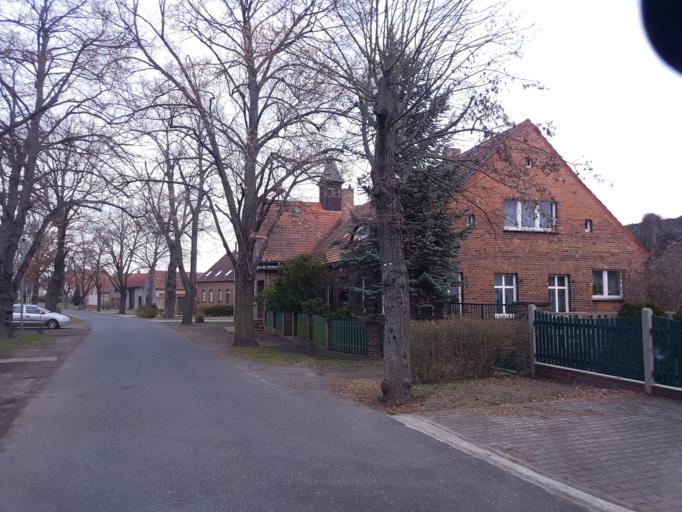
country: DE
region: Brandenburg
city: Finsterwalde
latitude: 51.6153
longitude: 13.7627
